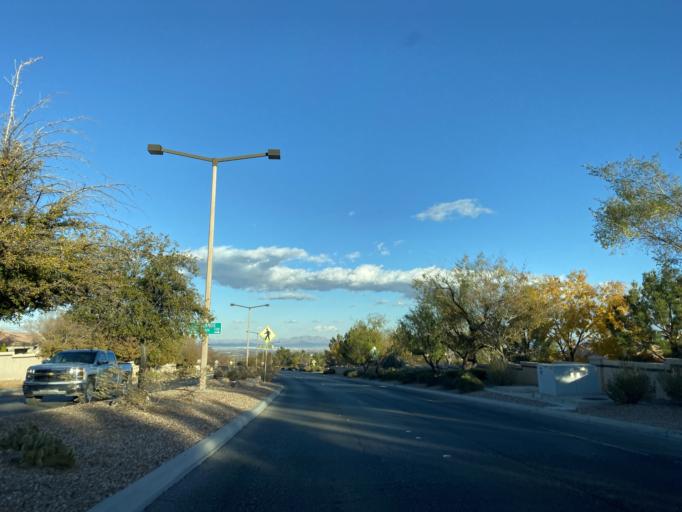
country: US
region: Nevada
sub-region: Clark County
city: Summerlin South
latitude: 36.2036
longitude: -115.3304
